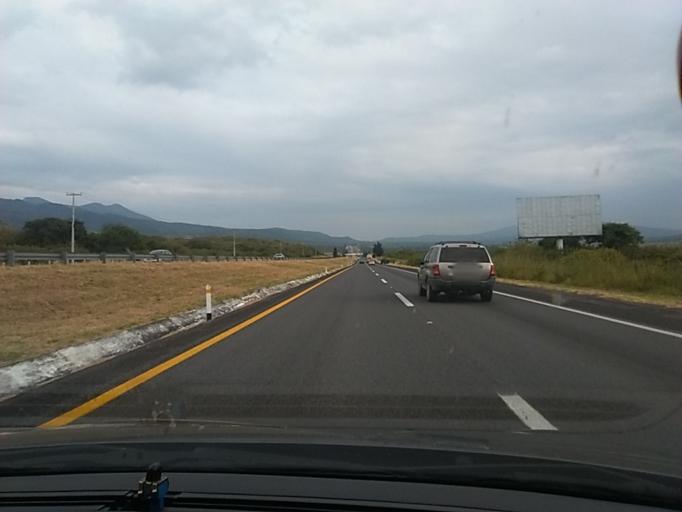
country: MX
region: Michoacan
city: Churintzio
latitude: 20.1412
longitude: -102.0816
